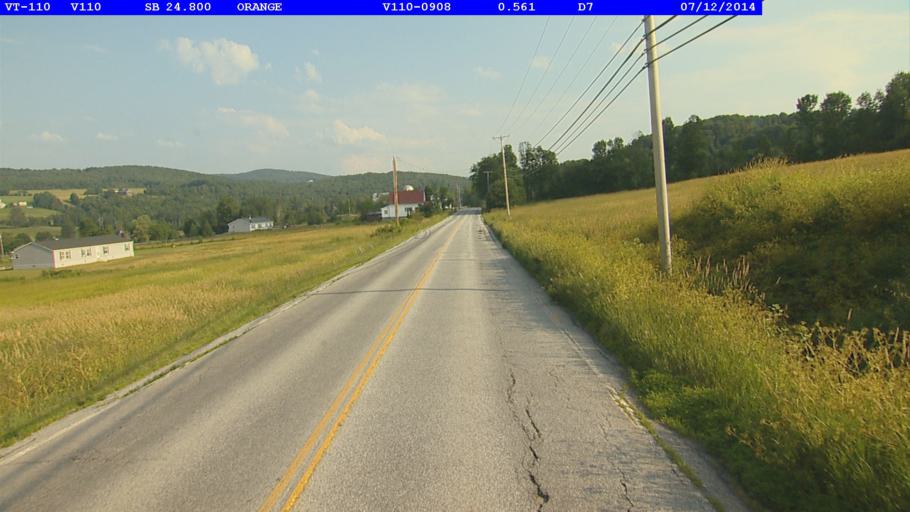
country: US
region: Vermont
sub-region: Washington County
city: South Barre
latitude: 44.1322
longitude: -72.4312
